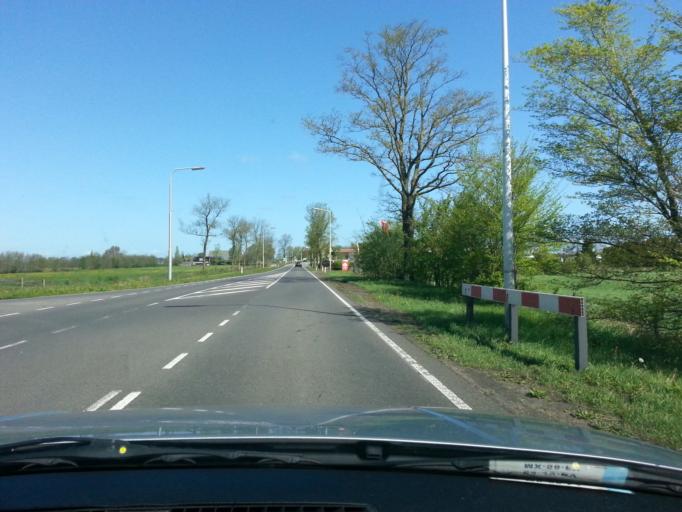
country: NL
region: Friesland
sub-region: Gemeente Achtkarspelen
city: Augustinusga
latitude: 53.2204
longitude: 6.1763
